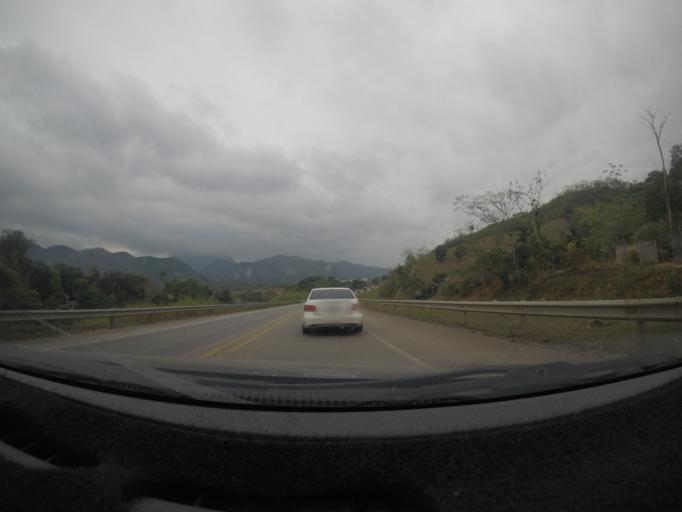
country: VN
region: Lao Cai
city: Thi Tran Khanh Yen
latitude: 22.1528
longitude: 104.3638
